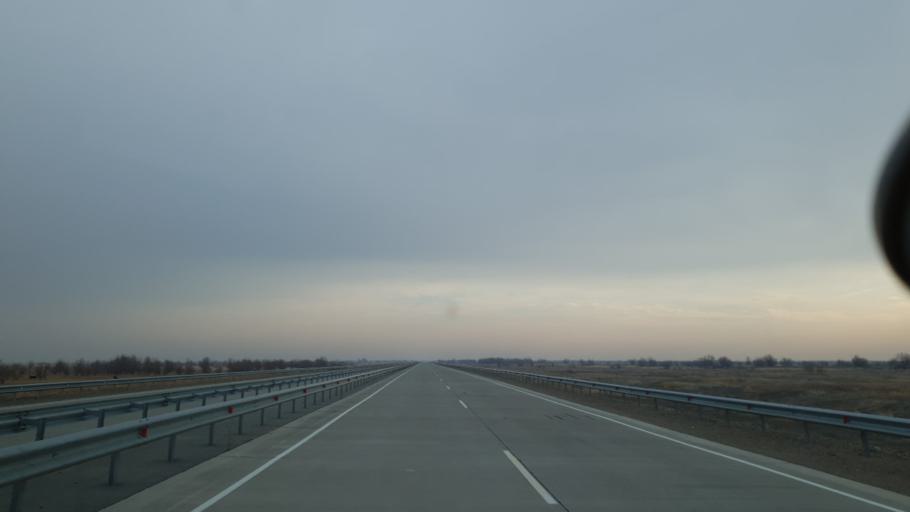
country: KZ
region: Almaty Oblysy
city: Zharkent
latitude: 44.0161
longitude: 79.7582
